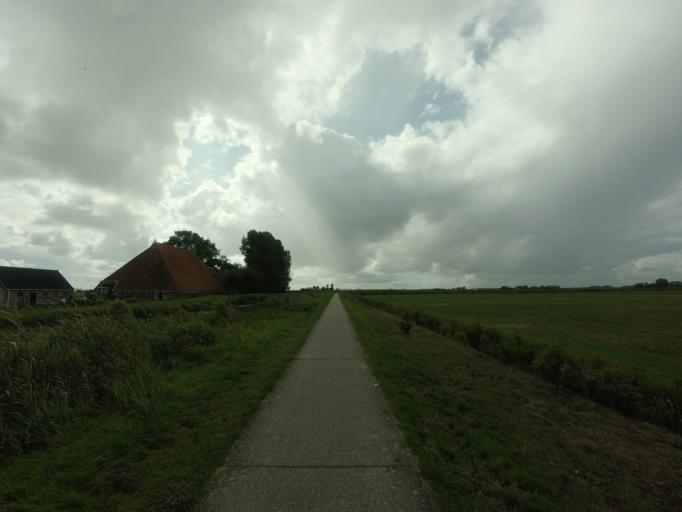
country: NL
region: Friesland
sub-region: Gemeente Leeuwarden
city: Wirdum
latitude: 53.1442
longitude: 5.8243
